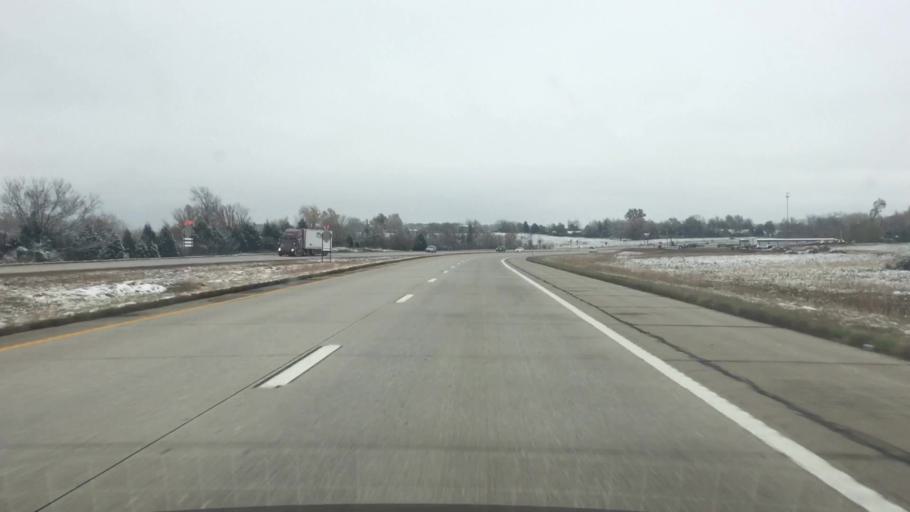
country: US
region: Missouri
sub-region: Saint Clair County
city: Osceola
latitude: 38.1781
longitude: -93.7247
